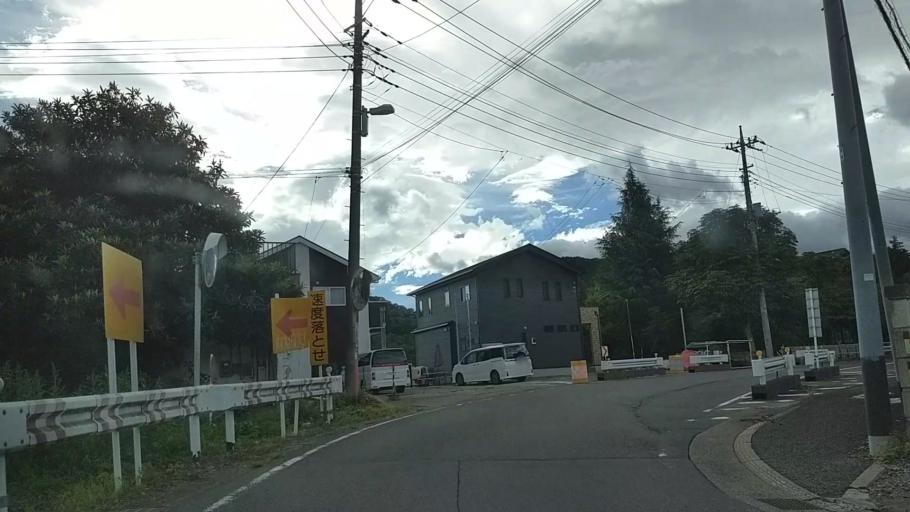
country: JP
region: Yamanashi
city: Uenohara
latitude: 35.5940
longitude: 139.1493
